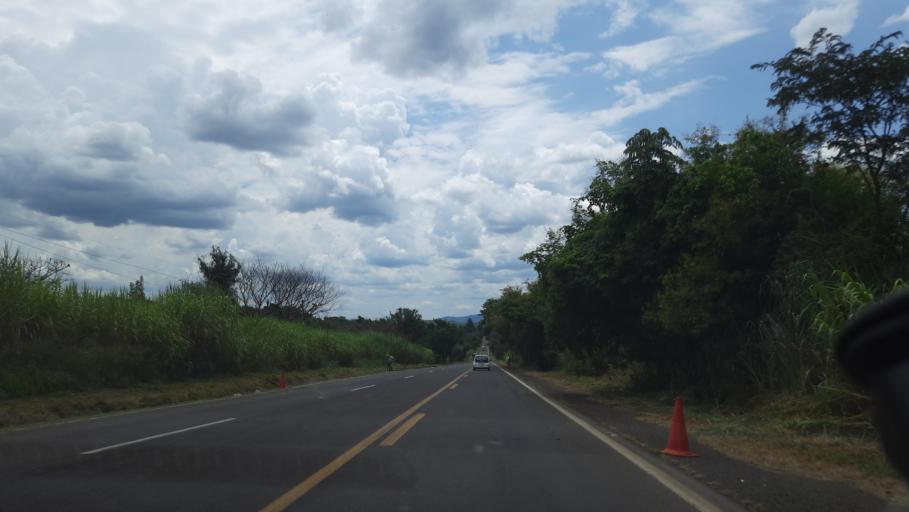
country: BR
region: Sao Paulo
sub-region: Mococa
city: Mococa
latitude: -21.4777
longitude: -47.0879
